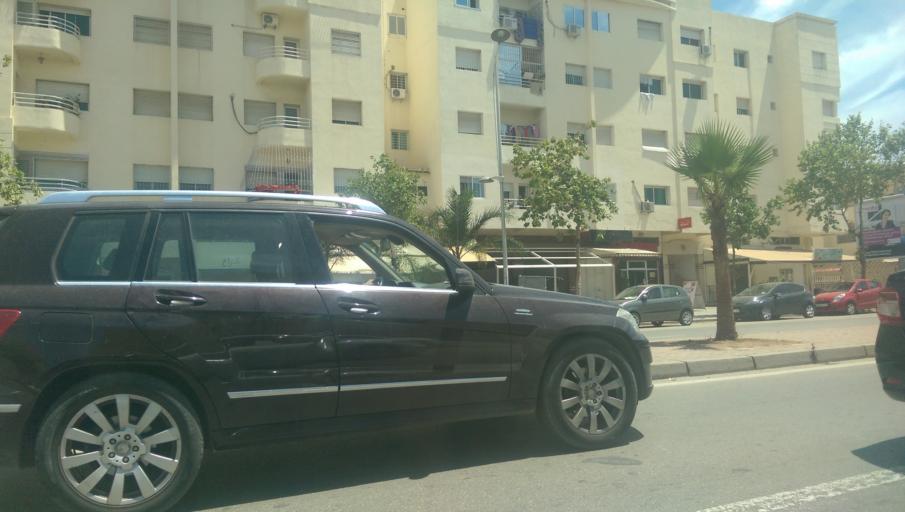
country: MA
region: Fes-Boulemane
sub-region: Fes
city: Fes
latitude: 34.0172
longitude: -4.9851
